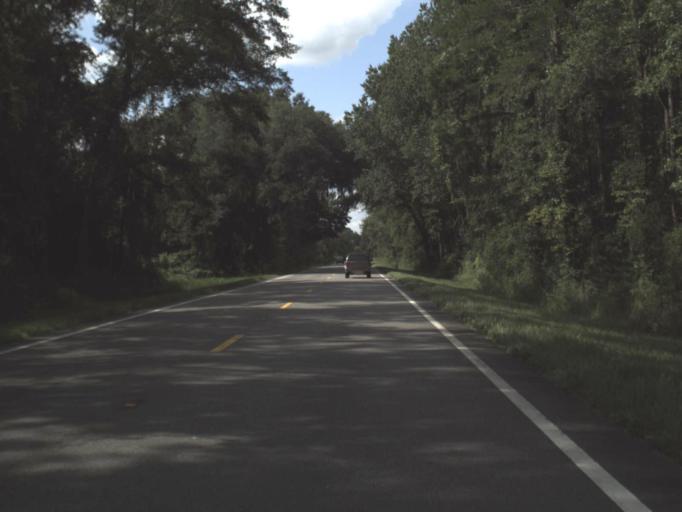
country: US
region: Florida
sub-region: Madison County
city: Madison
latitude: 30.3845
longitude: -83.6576
